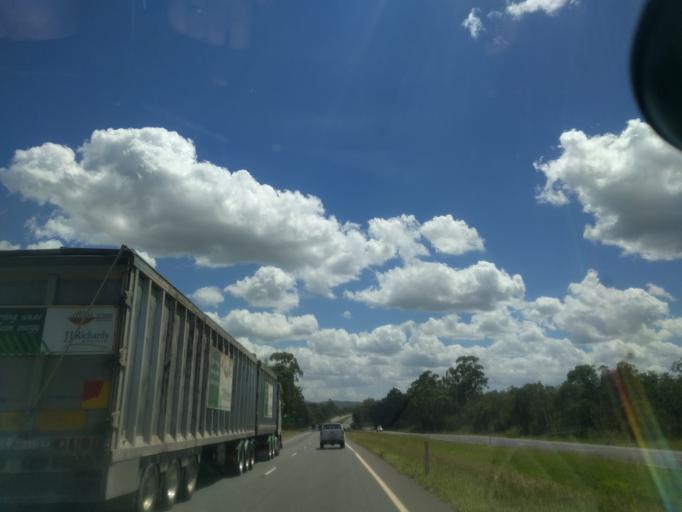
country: AU
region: Queensland
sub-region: Ipswich
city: Bundamba
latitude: -27.6085
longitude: 152.8292
